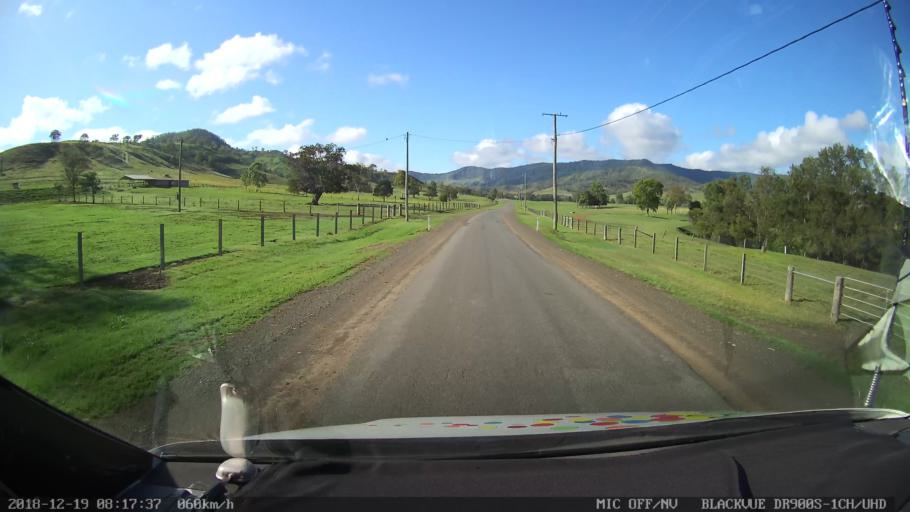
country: AU
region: New South Wales
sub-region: Kyogle
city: Kyogle
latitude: -28.2673
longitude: 152.9105
